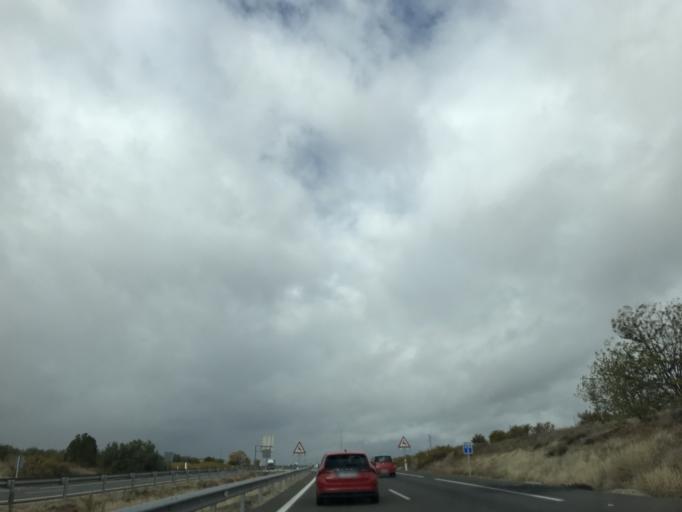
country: ES
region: Andalusia
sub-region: Provincia de Jaen
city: Bailen
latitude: 38.1067
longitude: -3.7457
